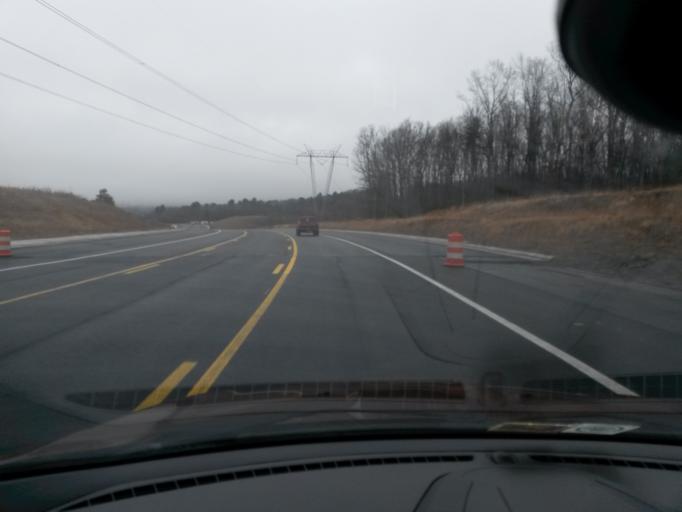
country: US
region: West Virginia
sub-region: Raleigh County
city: Stanaford
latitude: 37.8025
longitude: -81.1718
